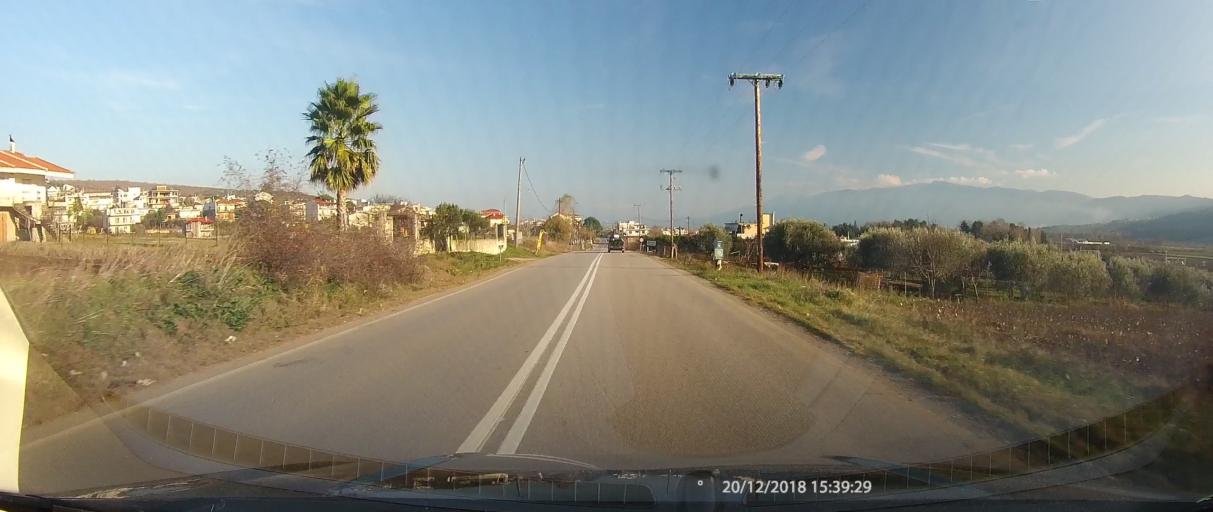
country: GR
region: Central Greece
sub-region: Nomos Fthiotidos
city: Stavros
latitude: 38.8960
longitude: 22.3652
